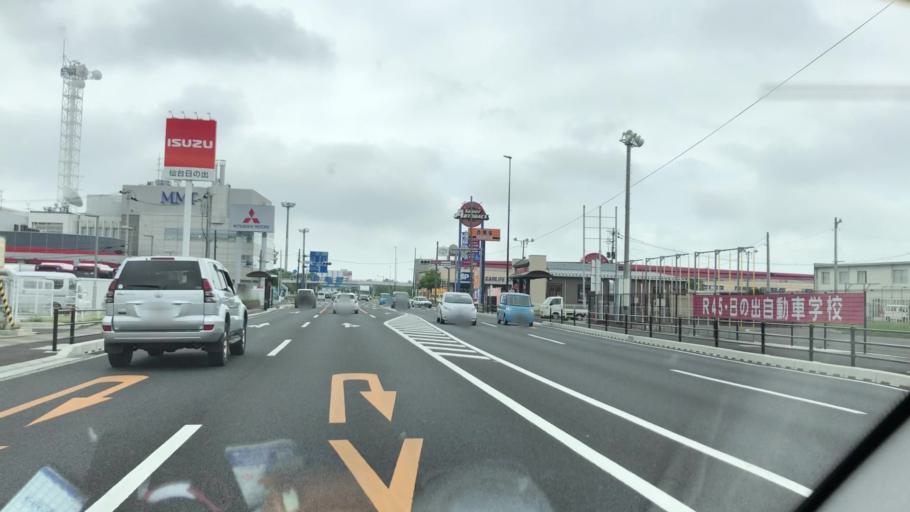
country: JP
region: Miyagi
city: Sendai-shi
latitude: 38.2694
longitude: 140.9333
